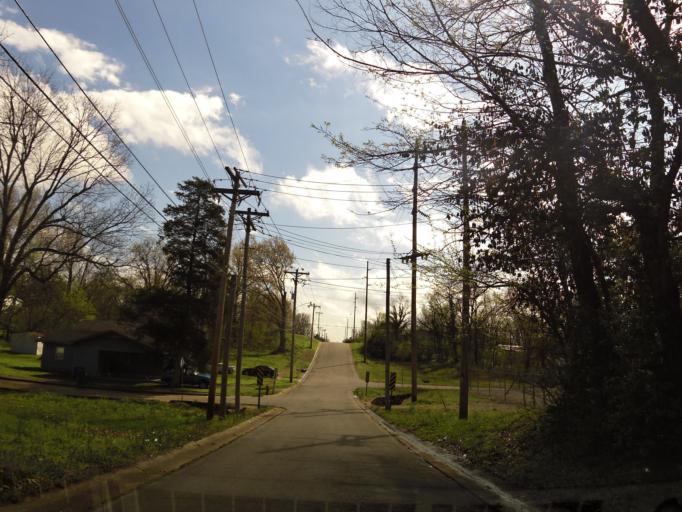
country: US
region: Missouri
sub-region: Butler County
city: Poplar Bluff
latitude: 36.7664
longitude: -90.3991
